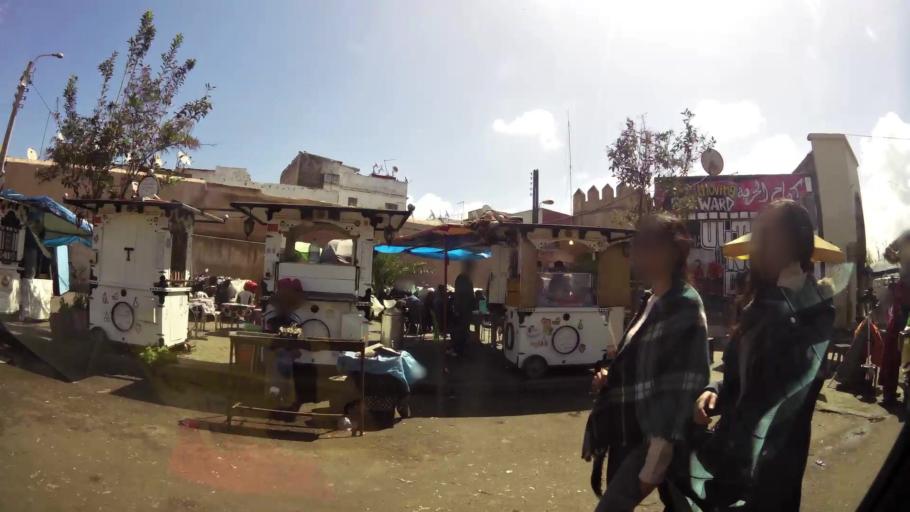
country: MA
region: Grand Casablanca
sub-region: Casablanca
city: Casablanca
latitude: 33.5970
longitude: -7.6207
